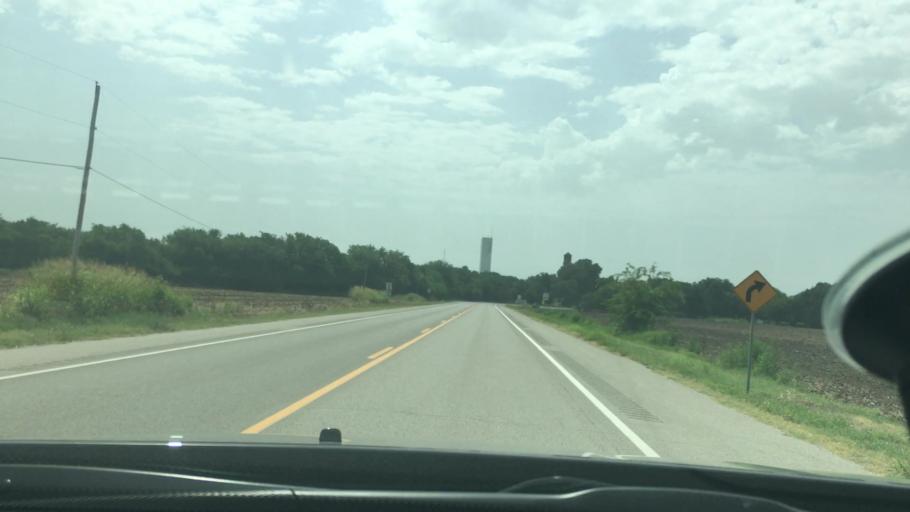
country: US
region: Oklahoma
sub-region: Garvin County
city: Pauls Valley
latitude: 34.8323
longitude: -97.2622
